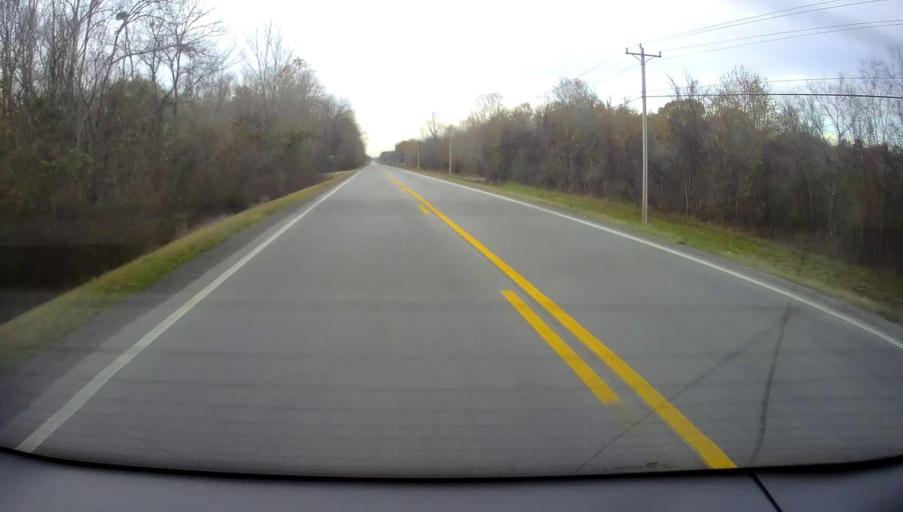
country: US
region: Alabama
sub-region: Morgan County
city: Falkville
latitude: 34.4200
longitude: -86.7117
